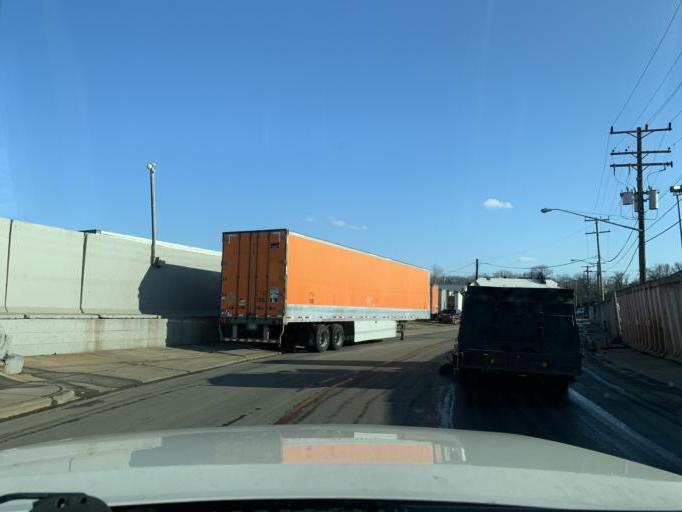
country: US
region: Maryland
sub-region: Prince George's County
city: Cheverly
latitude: 38.9147
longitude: -76.9307
